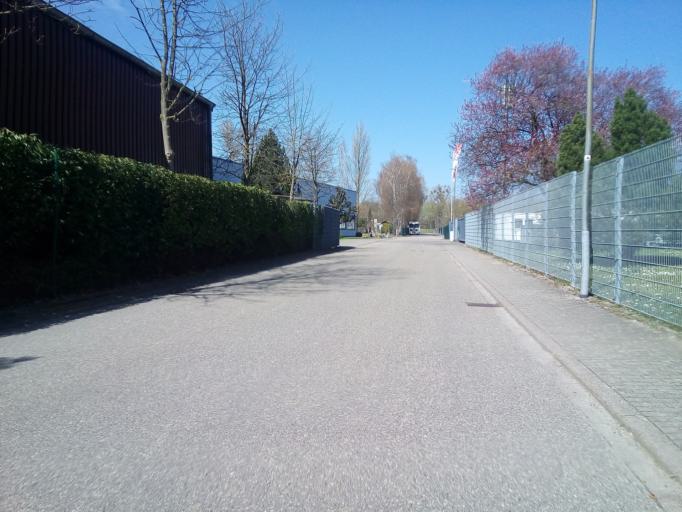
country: DE
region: Baden-Wuerttemberg
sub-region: Freiburg Region
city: Rheinau
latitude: 48.6811
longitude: 7.9373
